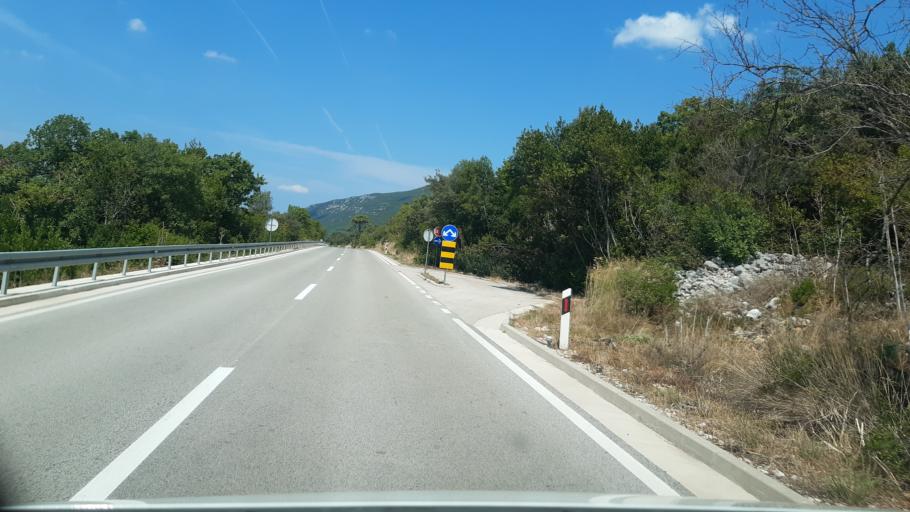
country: HR
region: Dubrovacko-Neretvanska
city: Ston
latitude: 42.8527
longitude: 17.7156
